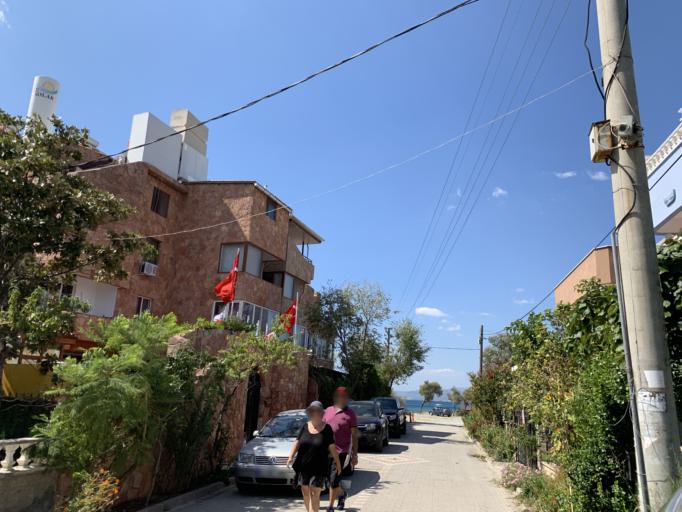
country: TR
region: Balikesir
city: Altinoluk
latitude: 39.5622
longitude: 26.8320
